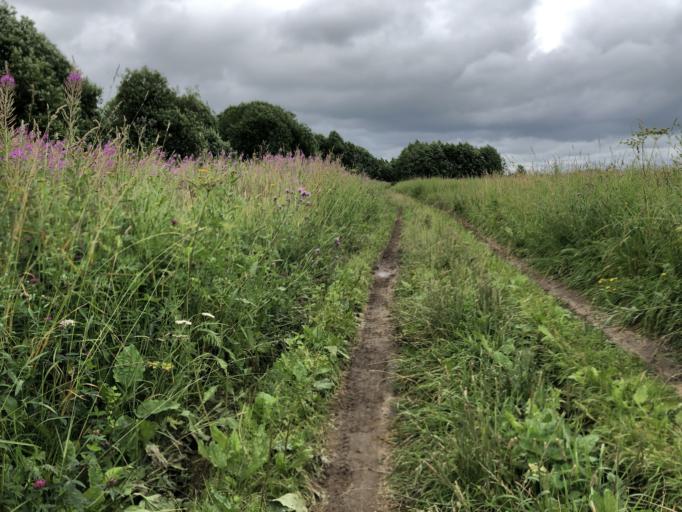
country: RU
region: Tverskaya
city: Rzhev
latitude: 56.2393
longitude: 34.3812
